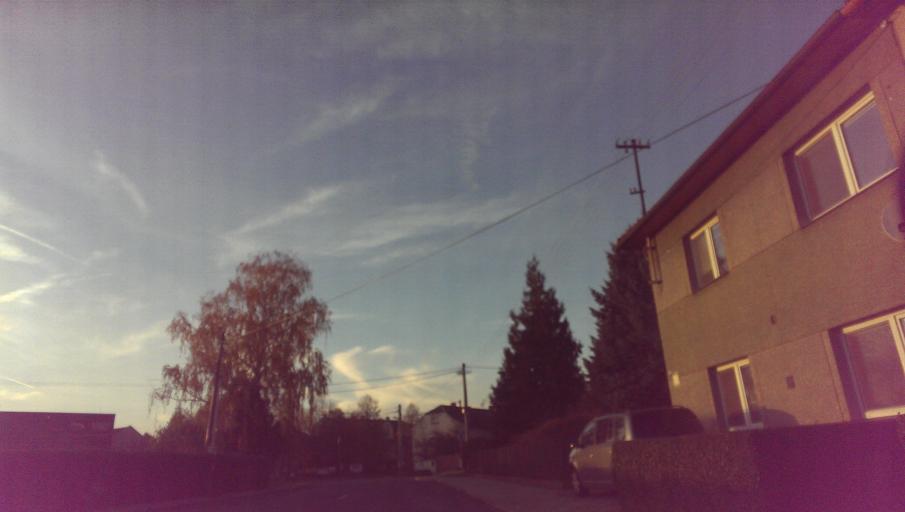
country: CZ
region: Zlin
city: Tecovice
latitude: 49.2165
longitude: 17.5893
